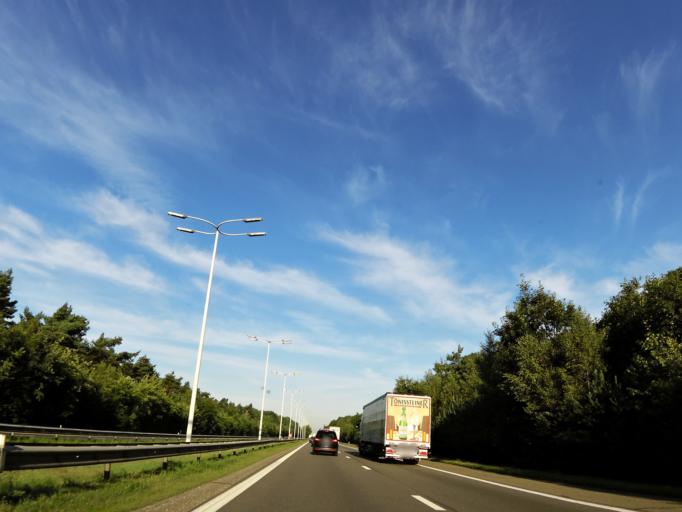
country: BE
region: Flanders
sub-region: Provincie Limburg
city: Zutendaal
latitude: 50.9679
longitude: 5.5895
